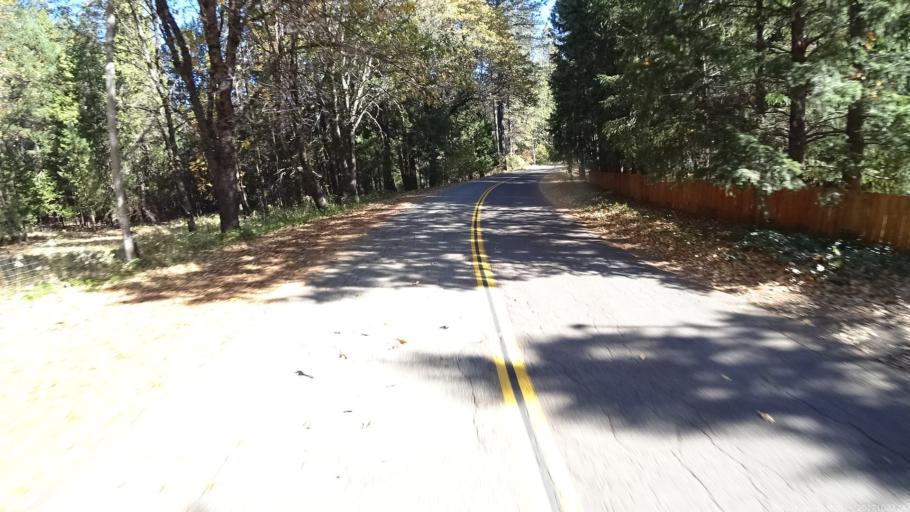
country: US
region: California
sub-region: Shasta County
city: Burney
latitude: 40.8259
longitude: -121.9525
